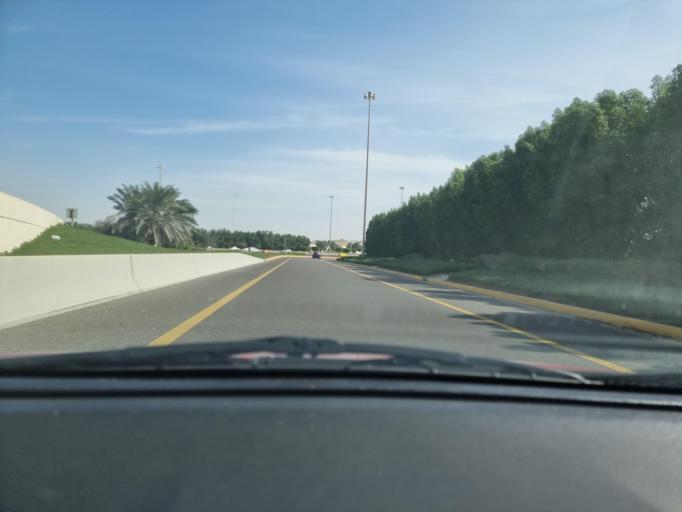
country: AE
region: Abu Dhabi
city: Abu Dhabi
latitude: 24.3262
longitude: 54.5846
